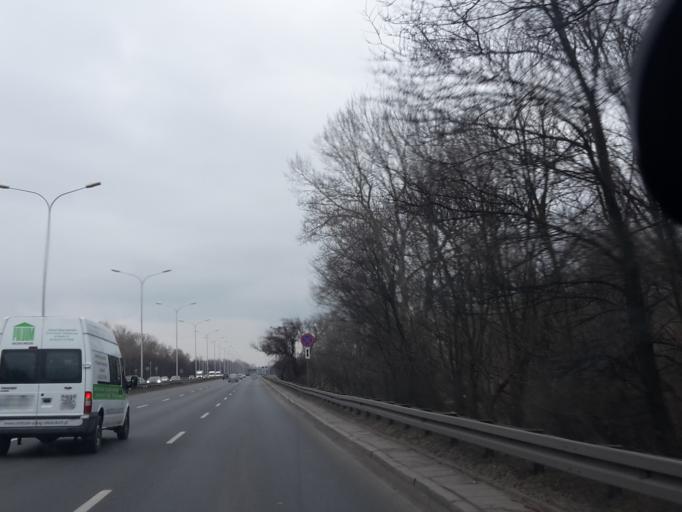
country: PL
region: Masovian Voivodeship
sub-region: Warszawa
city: Bialoleka
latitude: 52.2944
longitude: 20.9673
